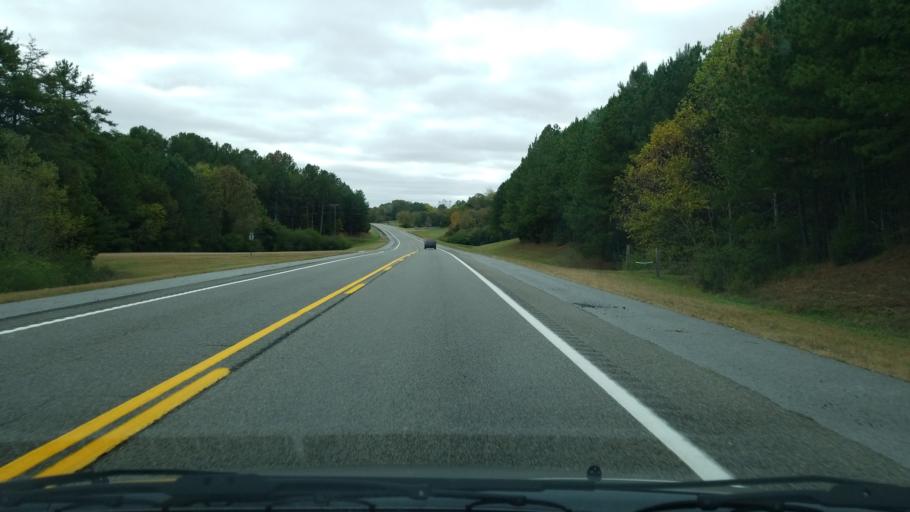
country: US
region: Tennessee
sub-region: Rhea County
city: Dayton
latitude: 35.4411
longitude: -85.0212
